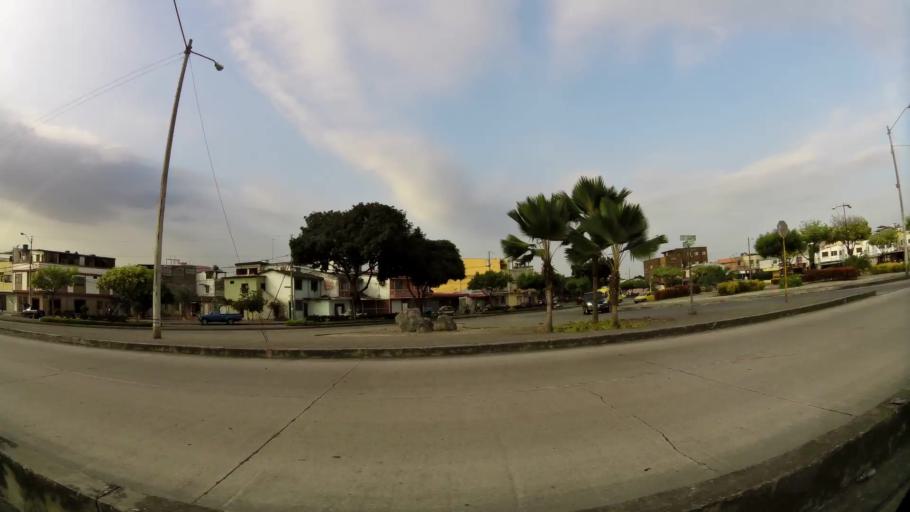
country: EC
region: Guayas
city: Eloy Alfaro
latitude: -2.1304
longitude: -79.8981
